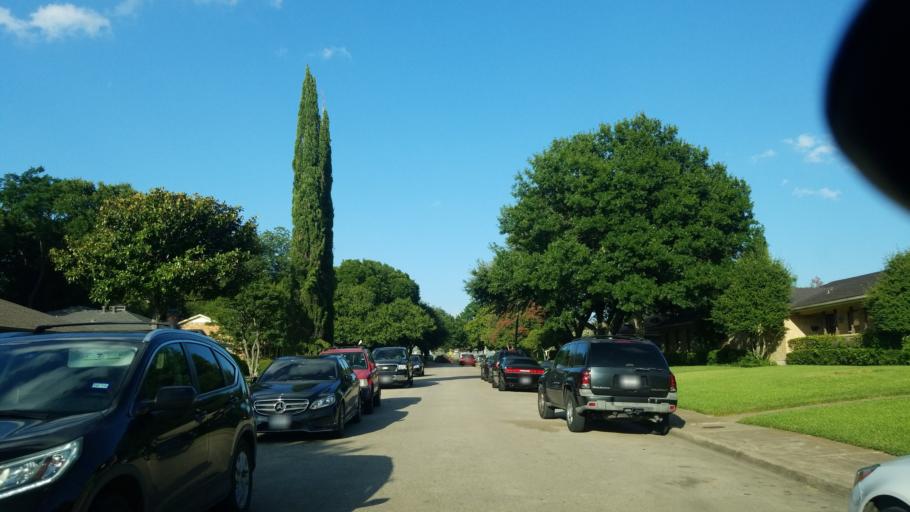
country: US
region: Texas
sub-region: Dallas County
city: Highland Park
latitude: 32.7854
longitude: -96.7104
